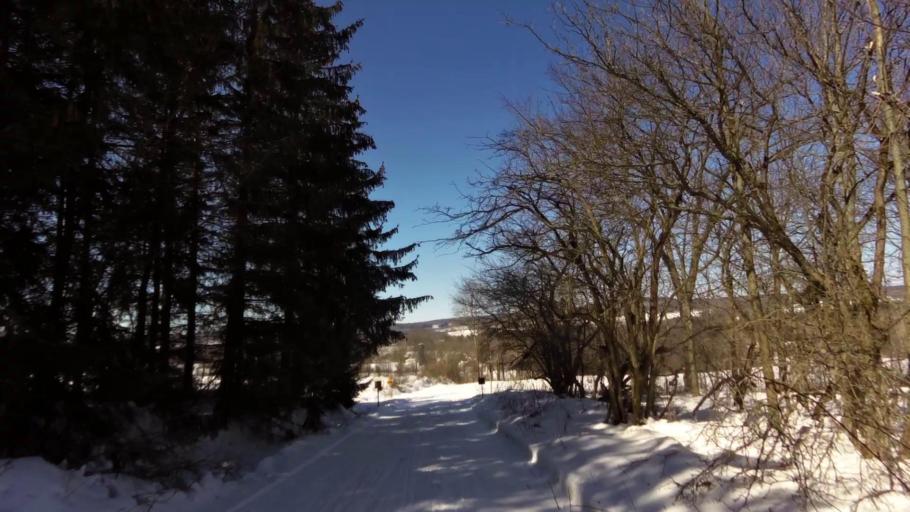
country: US
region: New York
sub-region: Allegany County
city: Houghton
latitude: 42.3794
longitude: -78.2489
